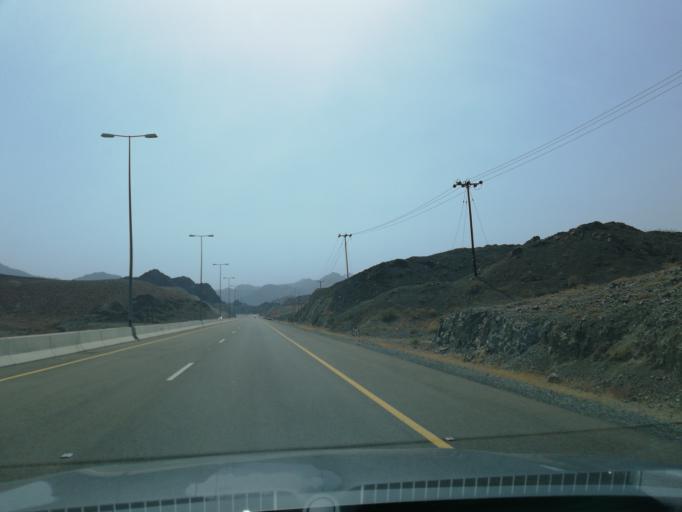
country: OM
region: Al Batinah
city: Al Liwa'
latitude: 24.2615
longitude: 56.3756
